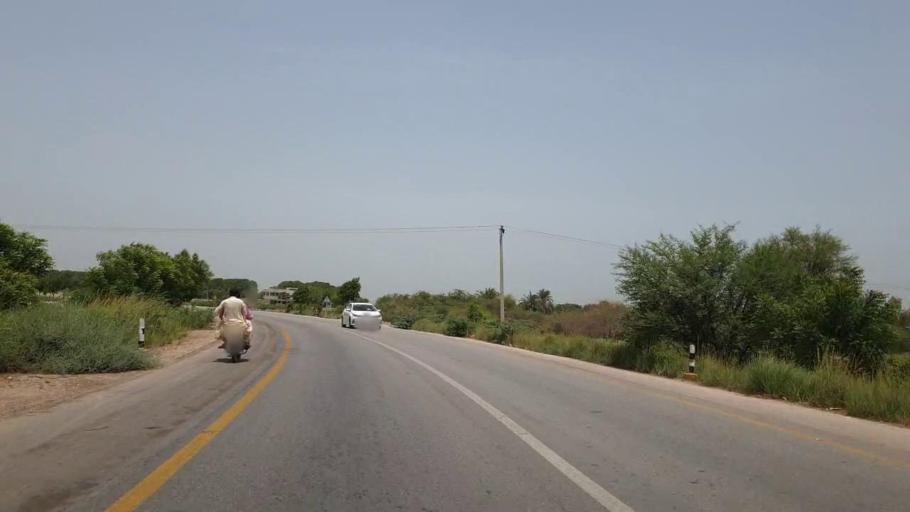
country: PK
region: Sindh
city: Nawabshah
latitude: 26.2458
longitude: 68.4631
